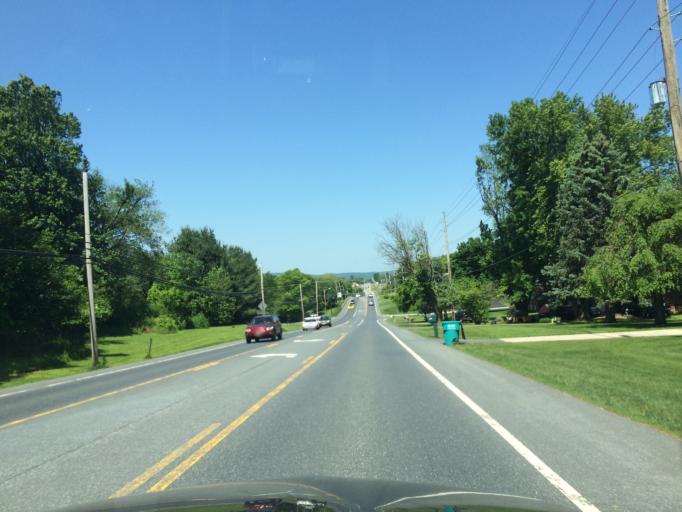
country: US
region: Maryland
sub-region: Frederick County
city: Braddock Heights
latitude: 39.4321
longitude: -77.5123
